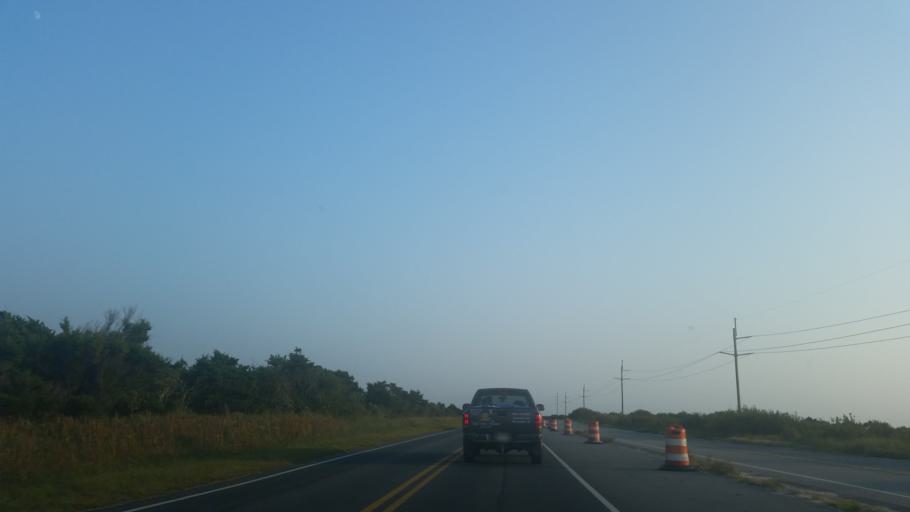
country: US
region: North Carolina
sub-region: Dare County
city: Wanchese
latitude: 35.6635
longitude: -75.4789
